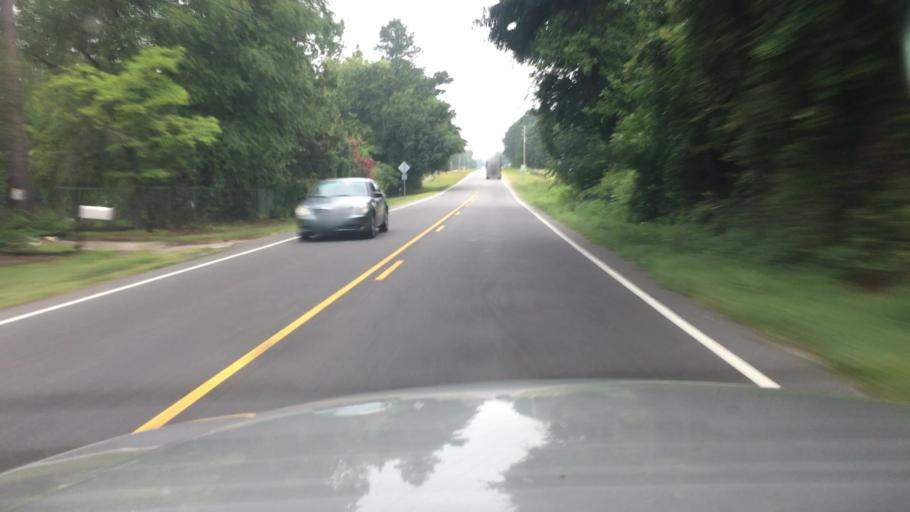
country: US
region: North Carolina
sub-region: Cumberland County
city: Hope Mills
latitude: 34.9749
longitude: -79.0026
